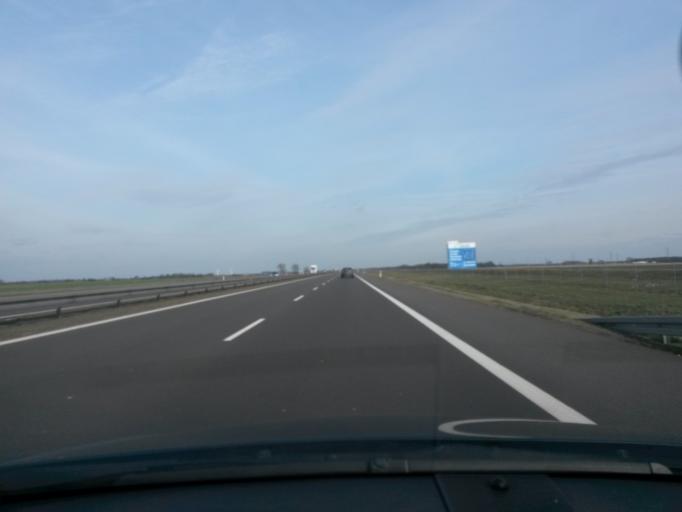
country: PL
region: Greater Poland Voivodeship
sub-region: Powiat sredzki
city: Dominowo
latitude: 52.3099
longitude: 17.3178
